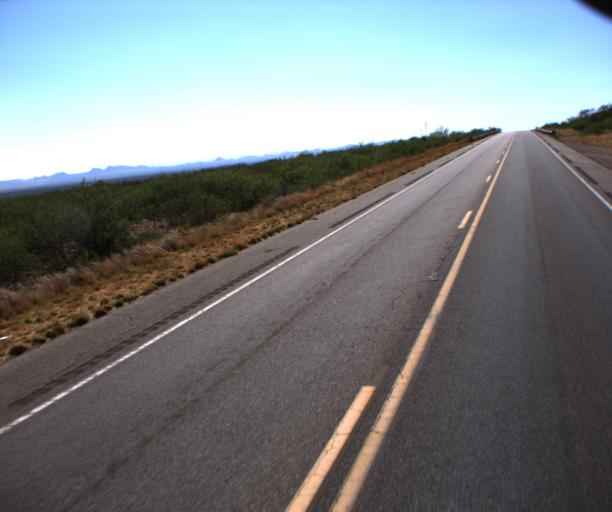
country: US
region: Arizona
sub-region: Cochise County
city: Bisbee
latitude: 31.4300
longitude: -109.8096
